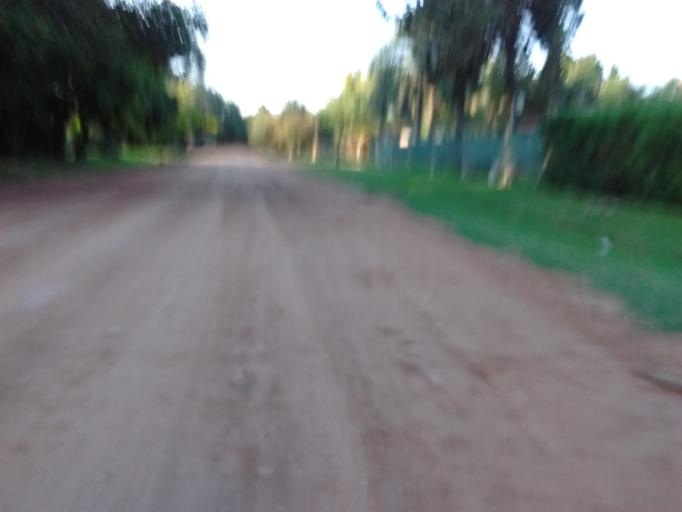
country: AR
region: Santa Fe
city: Funes
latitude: -32.9235
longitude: -60.8277
